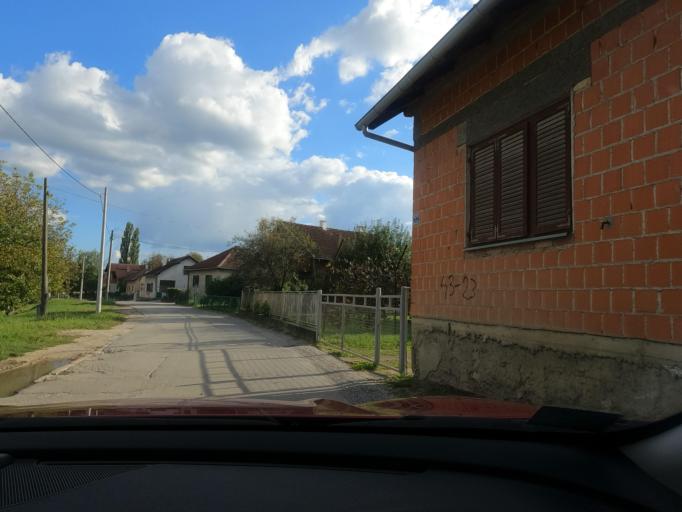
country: HR
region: Sisacko-Moslavacka
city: Petrinja
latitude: 45.4365
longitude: 16.2707
